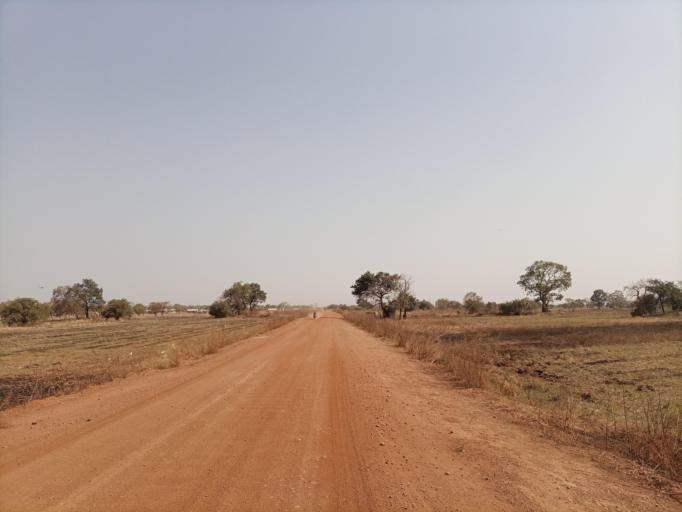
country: GH
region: Northern
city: Savelugu
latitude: 9.8118
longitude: -0.7752
